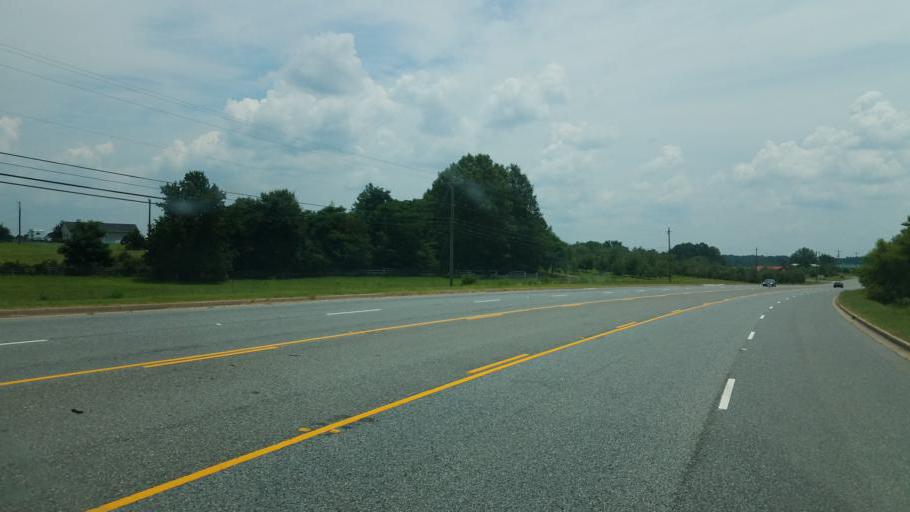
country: US
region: South Carolina
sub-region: York County
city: York
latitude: 35.0267
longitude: -81.2836
